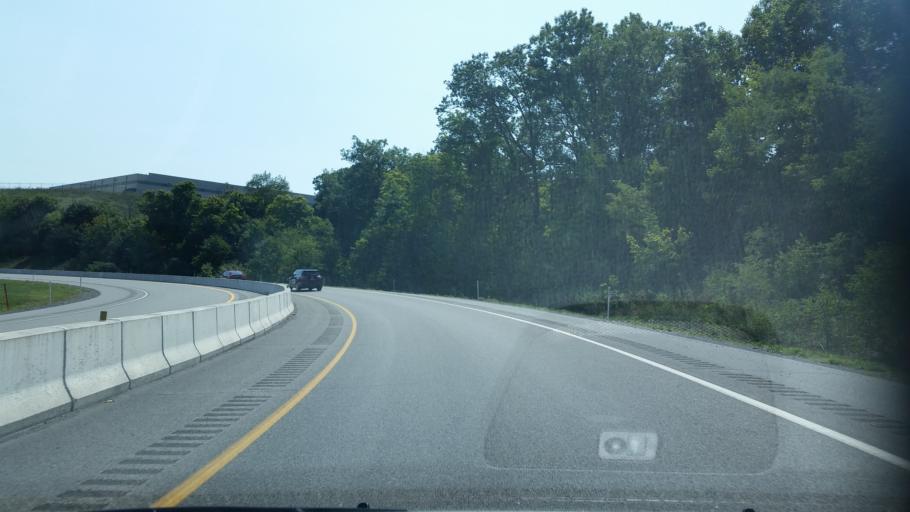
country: US
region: Pennsylvania
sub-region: Blair County
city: Duncansville
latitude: 40.4431
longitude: -78.4456
